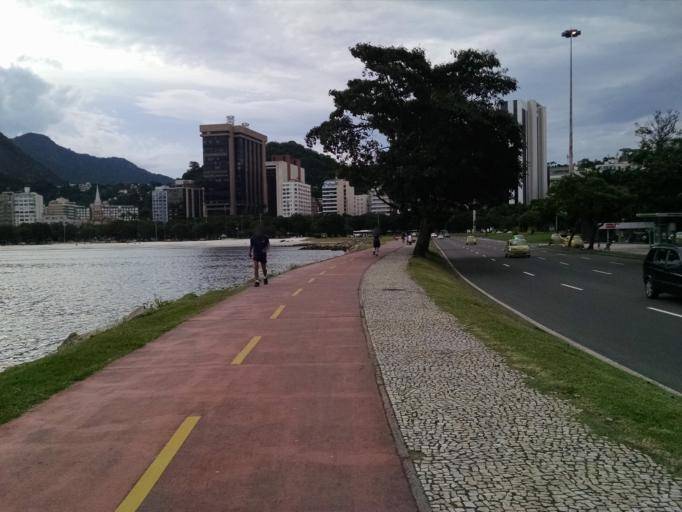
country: BR
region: Rio de Janeiro
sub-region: Rio De Janeiro
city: Rio de Janeiro
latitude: -22.9440
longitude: -43.1763
